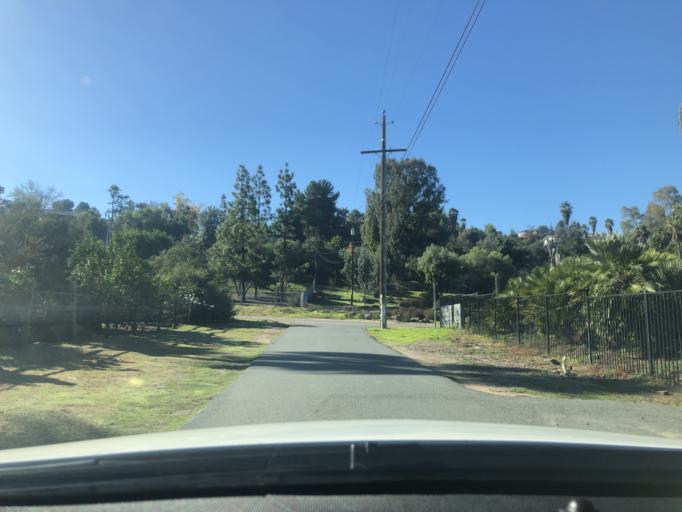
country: US
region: California
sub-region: San Diego County
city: El Cajon
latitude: 32.7775
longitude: -116.9432
